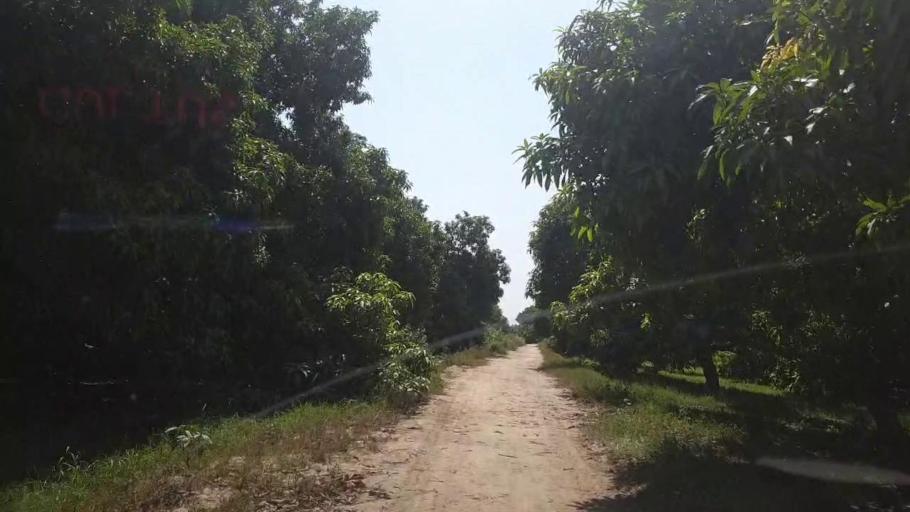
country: PK
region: Sindh
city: Tando Allahyar
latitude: 25.3944
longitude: 68.6696
